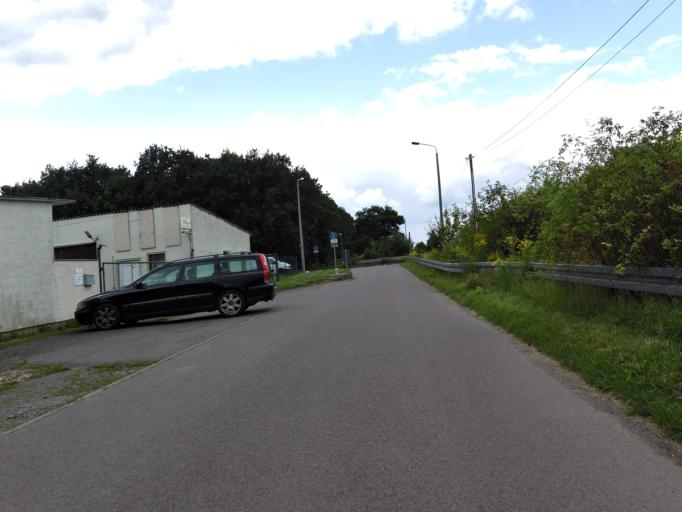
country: DE
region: Saxony
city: Rackwitz
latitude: 51.3873
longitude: 12.4096
